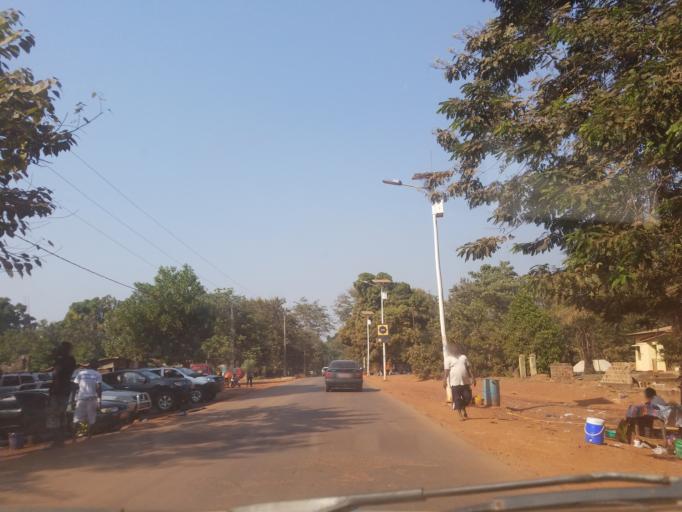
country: GN
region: Boke
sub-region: Boke Prefecture
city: Boke
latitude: 10.9221
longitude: -14.2955
